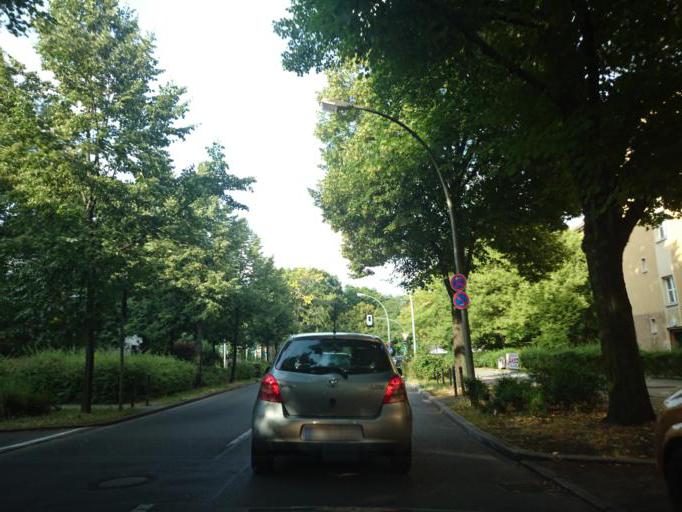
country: DE
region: Berlin
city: Plaenterwald
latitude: 52.4771
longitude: 13.4779
